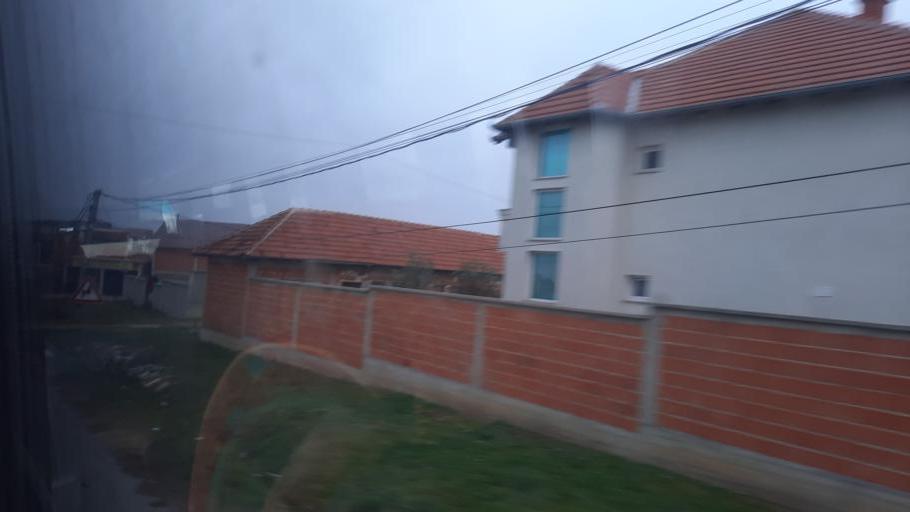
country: XK
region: Pristina
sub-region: Komuna e Drenasit
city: Glogovac
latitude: 42.6018
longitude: 20.8983
